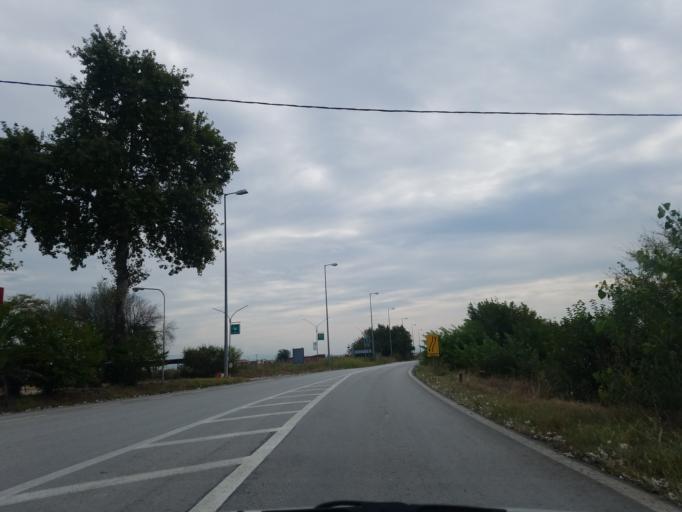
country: GR
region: Thessaly
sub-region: Nomos Kardhitsas
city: Sofades
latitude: 39.3220
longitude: 22.1099
